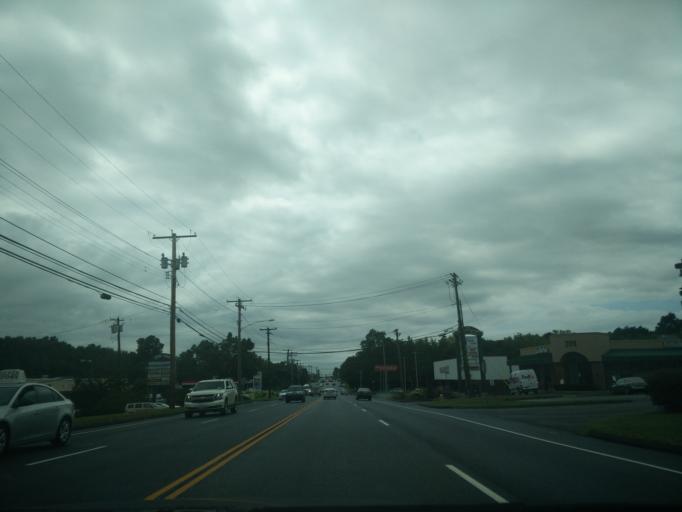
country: US
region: Connecticut
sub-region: New Haven County
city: Orange
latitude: 41.2611
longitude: -73.0084
